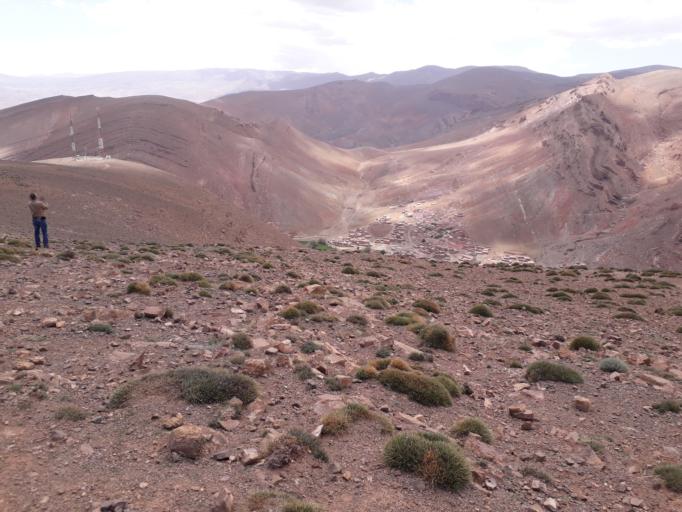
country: MA
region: Souss-Massa-Draa
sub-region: Ouarzazate
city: Tilmi
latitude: 31.8643
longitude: -5.7271
